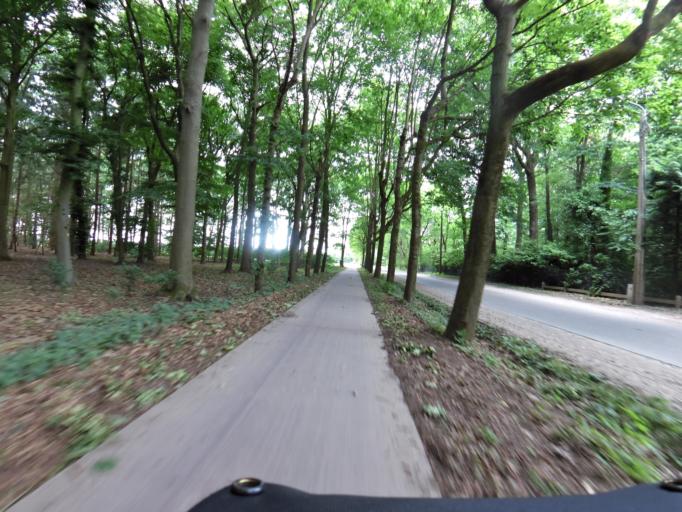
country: NL
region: North Brabant
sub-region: Gemeente Hilvarenbeek
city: Hilvarenbeek
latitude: 51.4317
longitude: 5.0792
